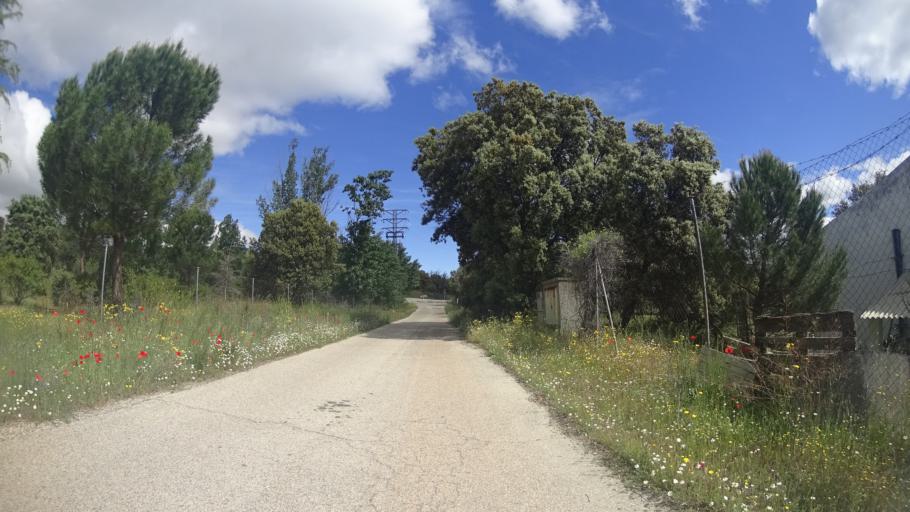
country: ES
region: Madrid
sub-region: Provincia de Madrid
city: Brunete
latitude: 40.4118
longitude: -3.9511
